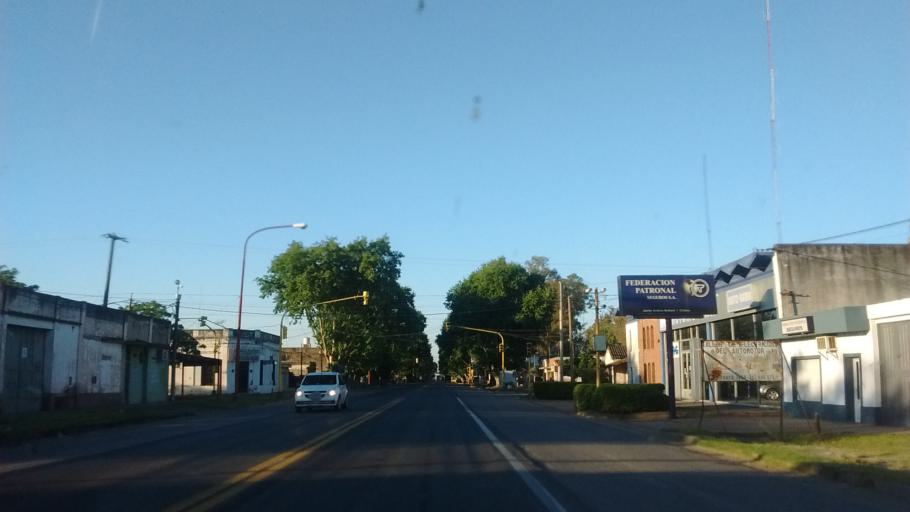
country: AR
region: Santa Fe
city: Firmat
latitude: -33.2408
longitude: -61.3557
